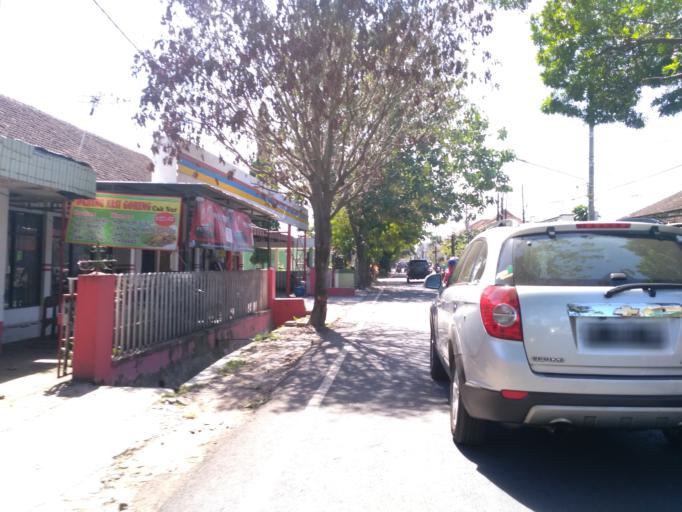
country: ID
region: East Java
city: Malang
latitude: -7.9820
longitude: 112.6478
